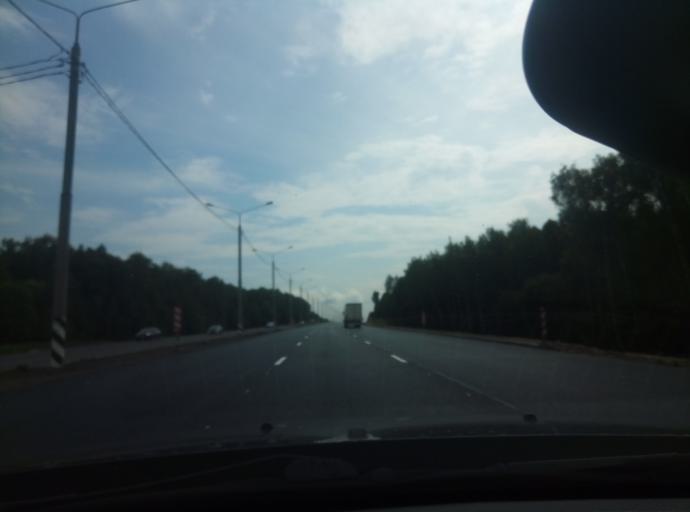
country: RU
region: Tula
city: Yasnogorsk
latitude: 54.5561
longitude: 37.5167
